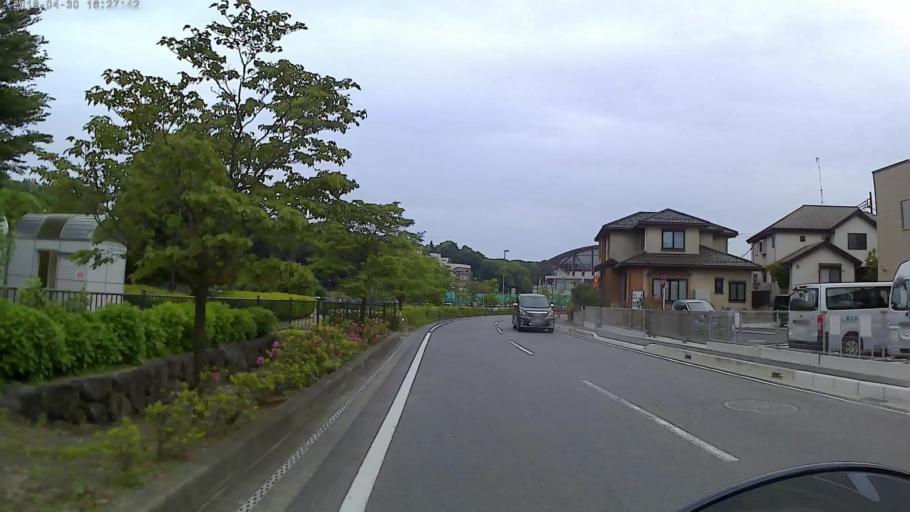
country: JP
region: Kanagawa
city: Zama
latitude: 35.4671
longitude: 139.4104
